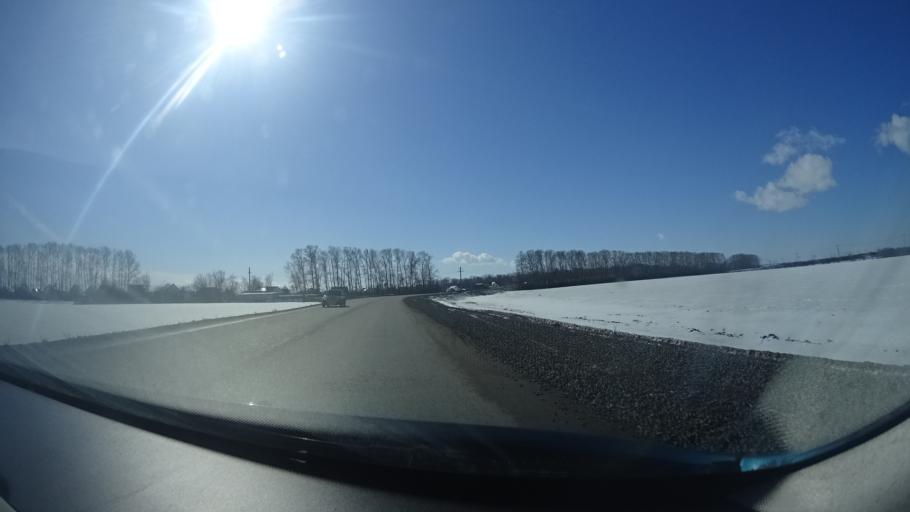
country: RU
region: Bashkortostan
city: Ufa
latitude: 54.6139
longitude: 55.8907
